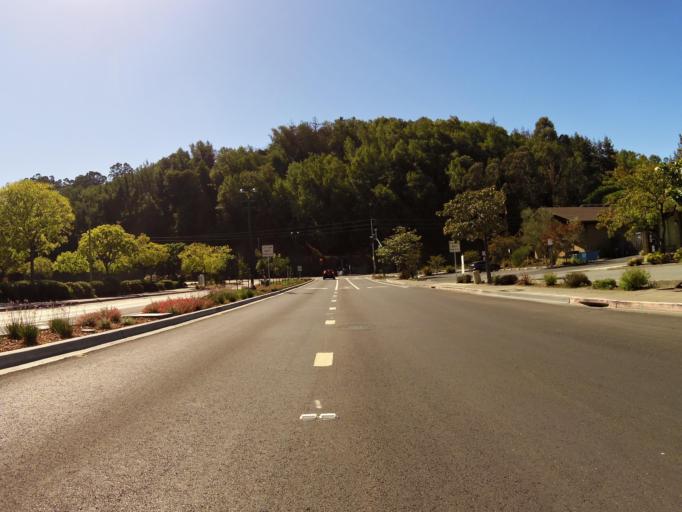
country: US
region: California
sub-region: Marin County
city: Larkspur
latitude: 37.9438
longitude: -122.5396
